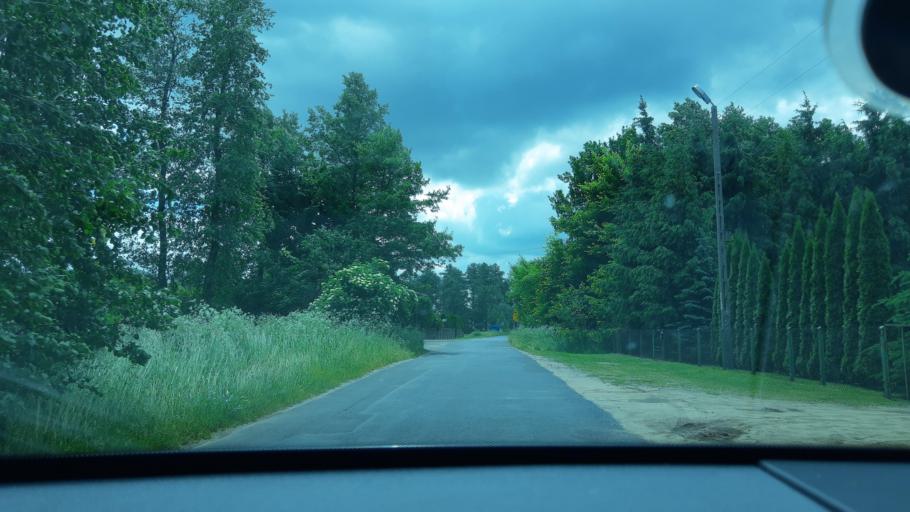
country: PL
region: Lodz Voivodeship
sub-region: Powiat zdunskowolski
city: Zapolice
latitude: 51.5301
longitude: 18.8377
